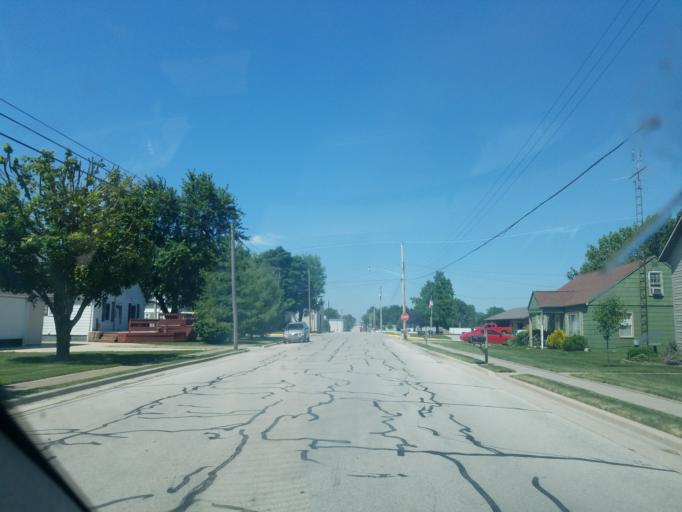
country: US
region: Ohio
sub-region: Mercer County
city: Saint Henry
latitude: 40.4214
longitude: -84.6397
